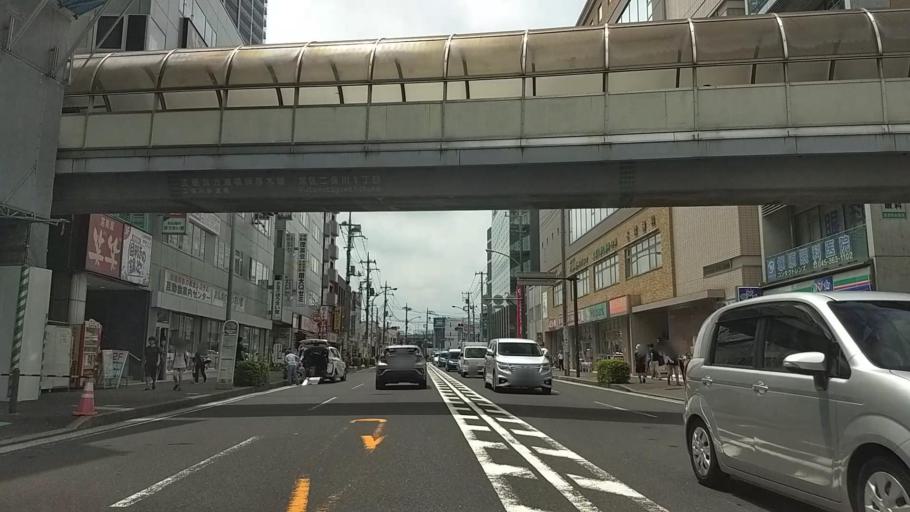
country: JP
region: Kanagawa
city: Minami-rinkan
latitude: 35.4637
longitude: 139.5318
